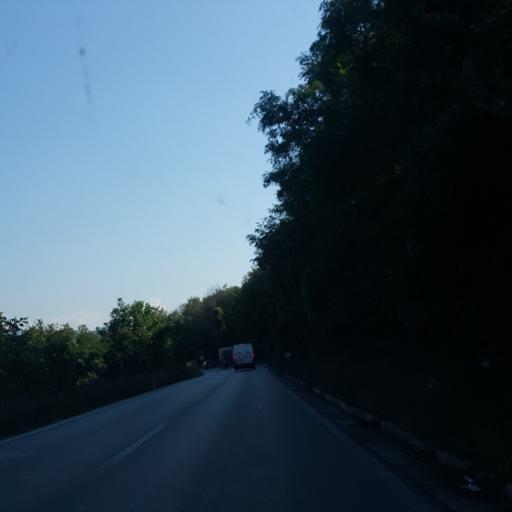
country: RS
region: Central Serbia
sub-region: Nisavski Okrug
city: Niska Banja
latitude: 43.3690
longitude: 22.0464
